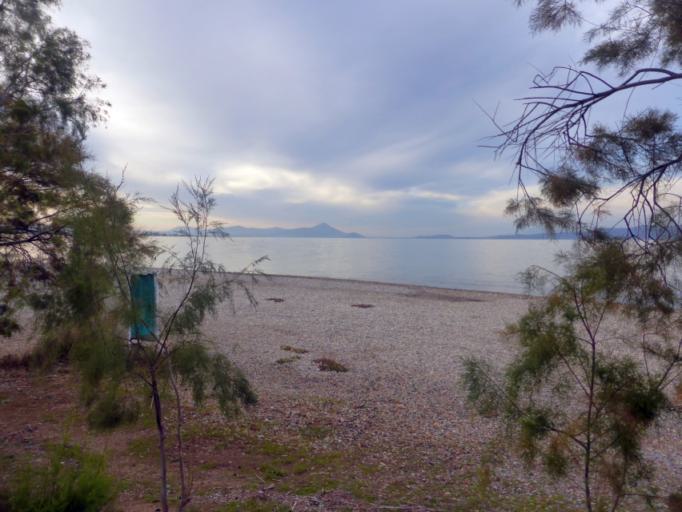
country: GR
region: Attica
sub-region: Nomarchia Anatolikis Attikis
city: Nea Palatia
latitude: 38.3283
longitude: 23.8076
